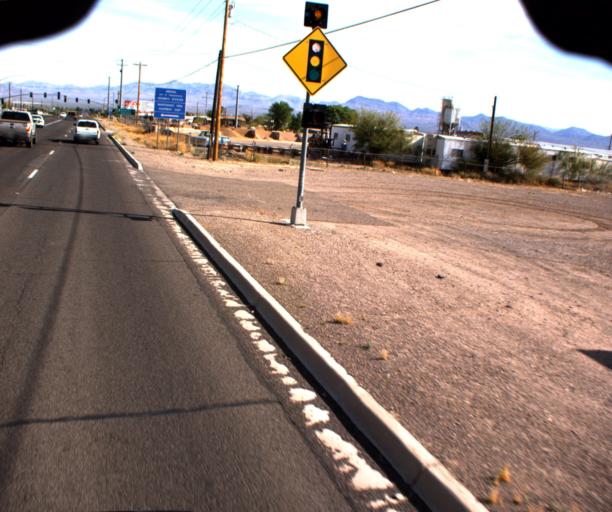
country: US
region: Arizona
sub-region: Graham County
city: Safford
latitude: 32.8006
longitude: -109.7077
